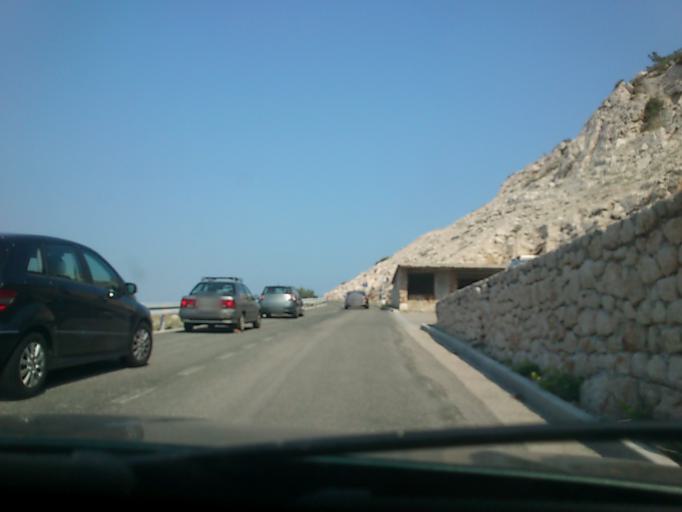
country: HR
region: Primorsko-Goranska
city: Banjol
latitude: 44.7065
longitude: 14.8951
